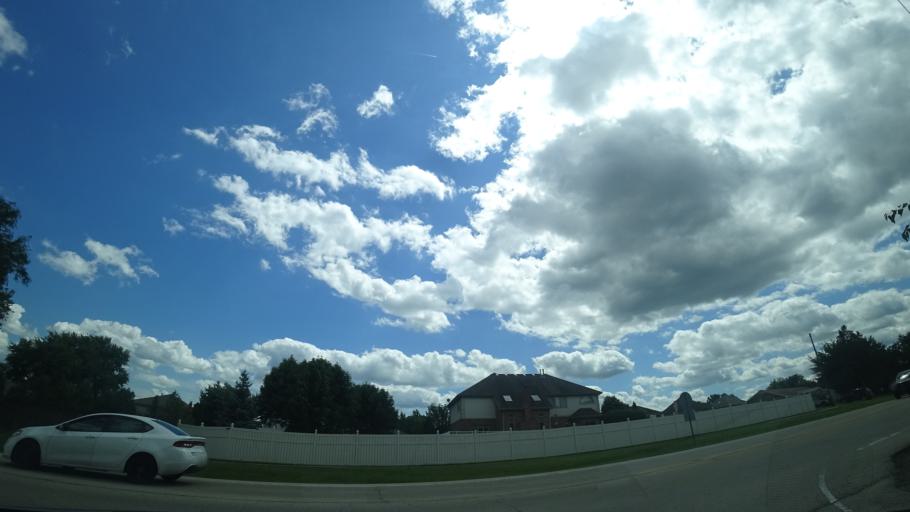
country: US
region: Illinois
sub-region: Cook County
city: Orland Hills
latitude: 41.5863
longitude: -87.8863
